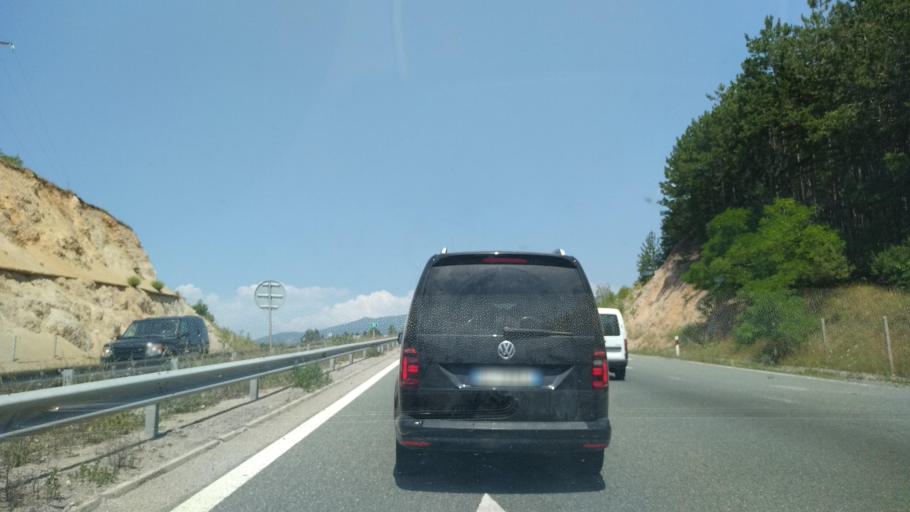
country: BG
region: Pernik
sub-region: Obshtina Pernik
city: Pernik
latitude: 42.4971
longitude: 23.1370
